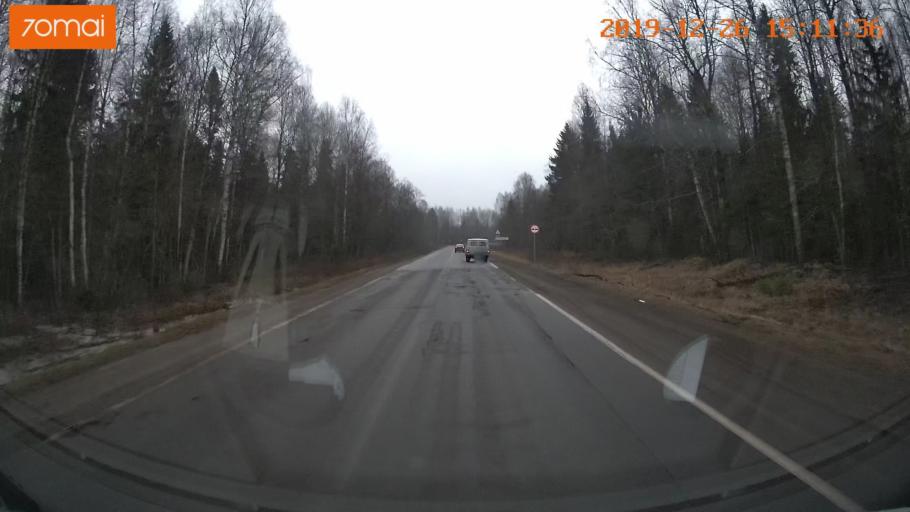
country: RU
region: Jaroslavl
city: Rybinsk
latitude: 58.1337
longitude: 38.8641
